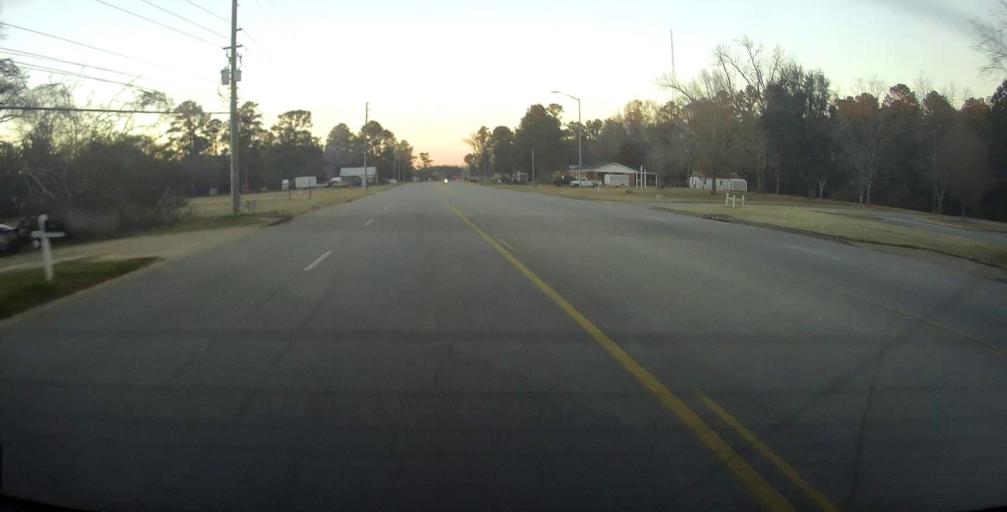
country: US
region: Georgia
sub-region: Dougherty County
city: Albany
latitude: 31.5438
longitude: -84.1366
